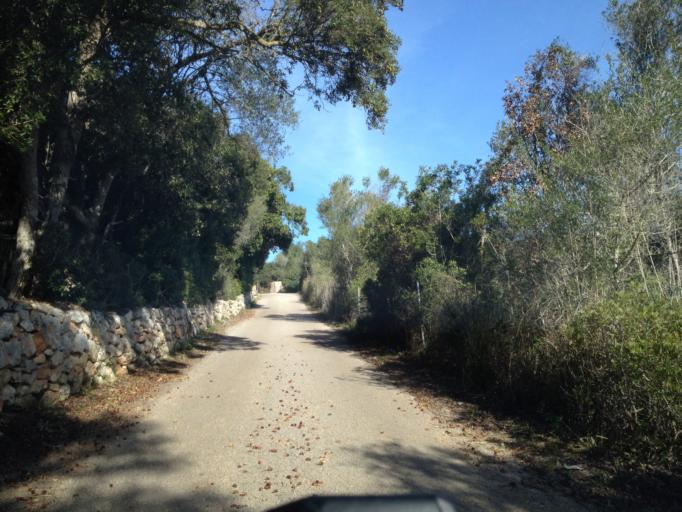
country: ES
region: Balearic Islands
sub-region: Illes Balears
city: Son Servera
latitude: 39.6103
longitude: 3.3395
